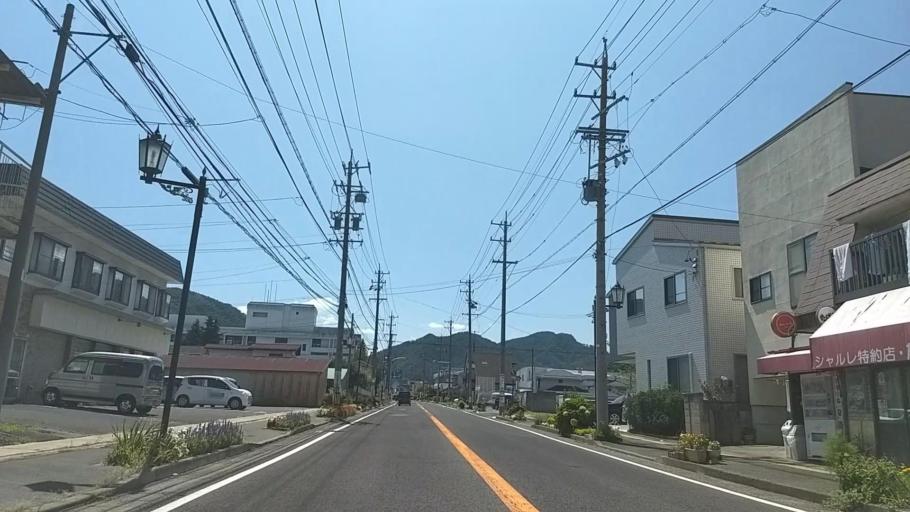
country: JP
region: Nagano
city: Kamimaruko
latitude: 36.3258
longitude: 138.2700
